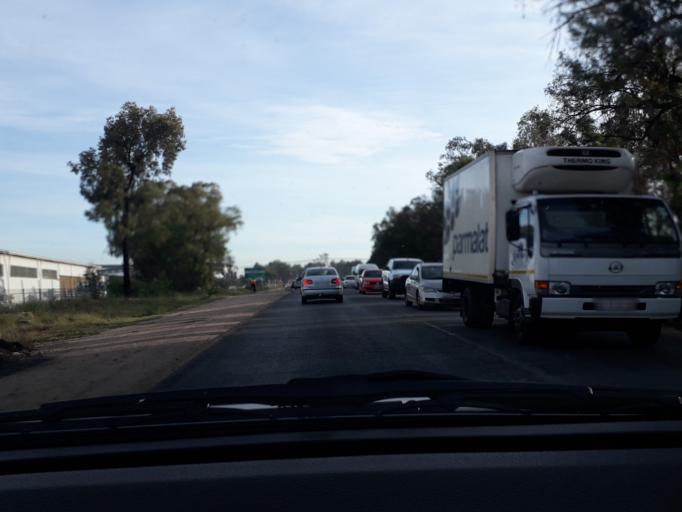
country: ZA
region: Gauteng
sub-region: City of Johannesburg Metropolitan Municipality
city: Midrand
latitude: -25.9281
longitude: 28.1497
